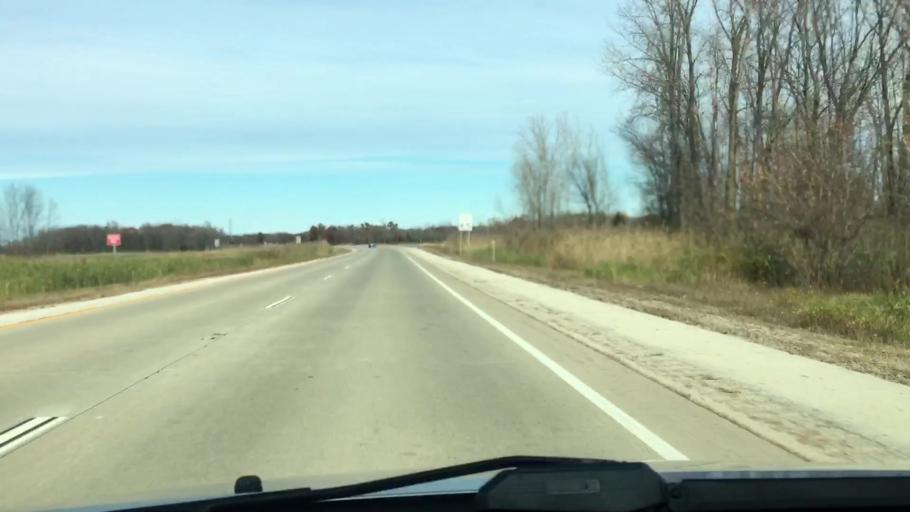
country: US
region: Wisconsin
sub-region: Brown County
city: Bellevue
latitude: 44.5823
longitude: -87.8697
